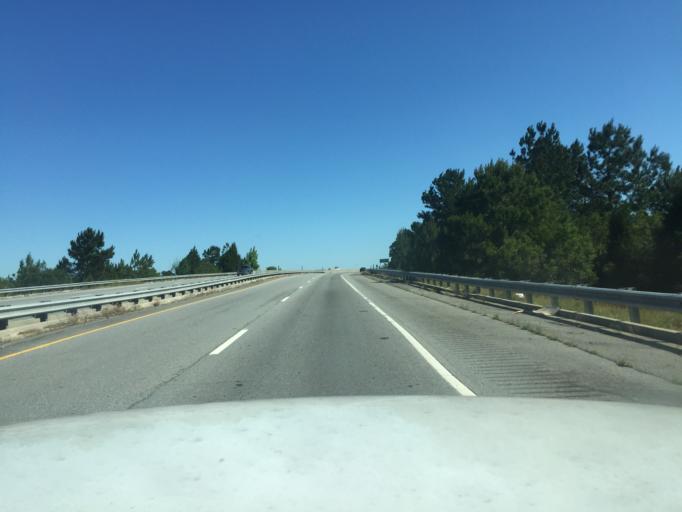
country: US
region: Georgia
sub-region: Chatham County
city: Georgetown
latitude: 31.9977
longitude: -81.2006
